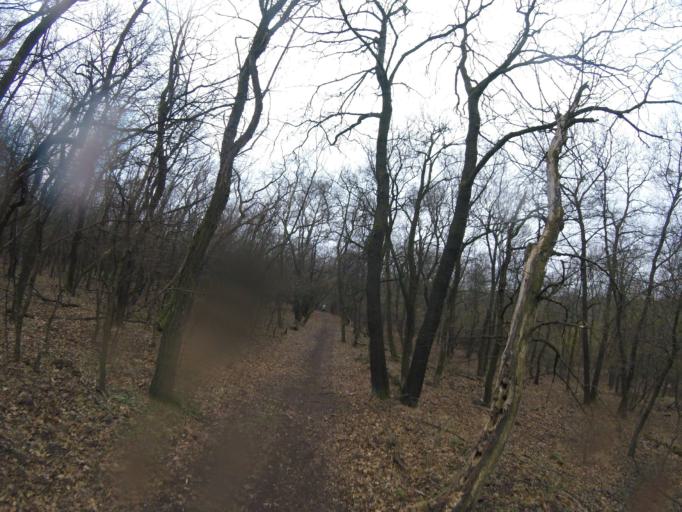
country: HU
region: Pest
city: Szob
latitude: 47.8091
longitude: 18.8267
